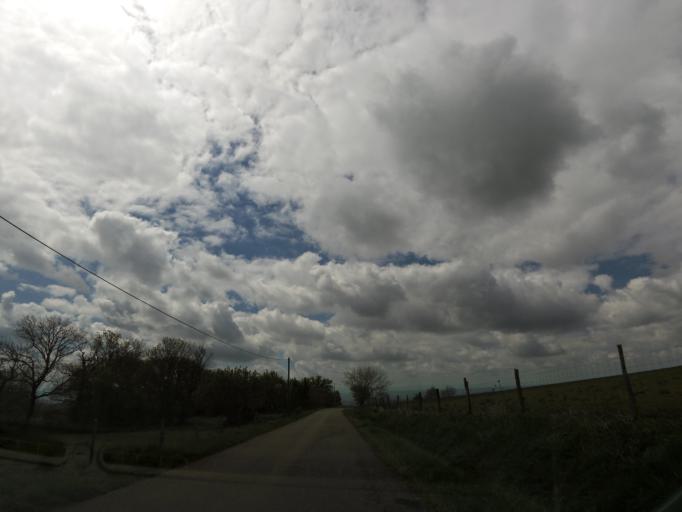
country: FR
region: Languedoc-Roussillon
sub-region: Departement de l'Aude
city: Villepinte
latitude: 43.3566
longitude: 2.1493
